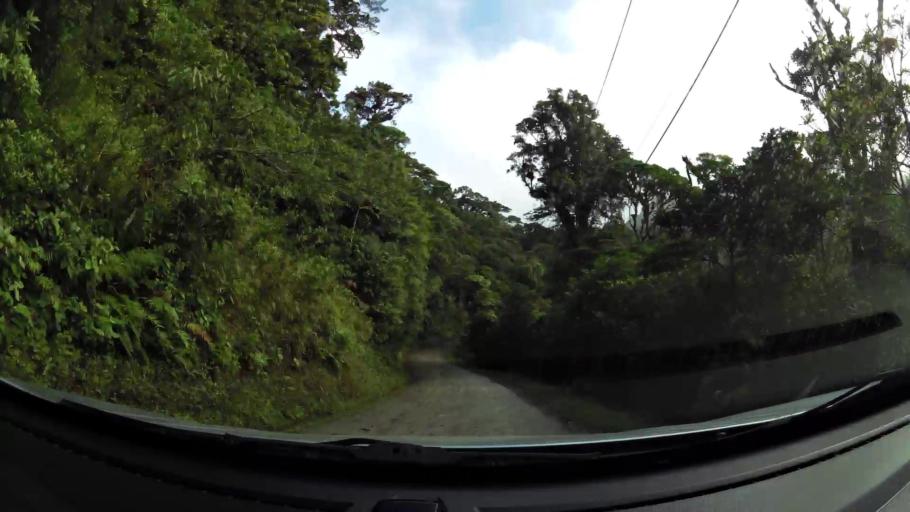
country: CR
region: Guanacaste
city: Juntas
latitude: 10.3006
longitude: -84.7969
